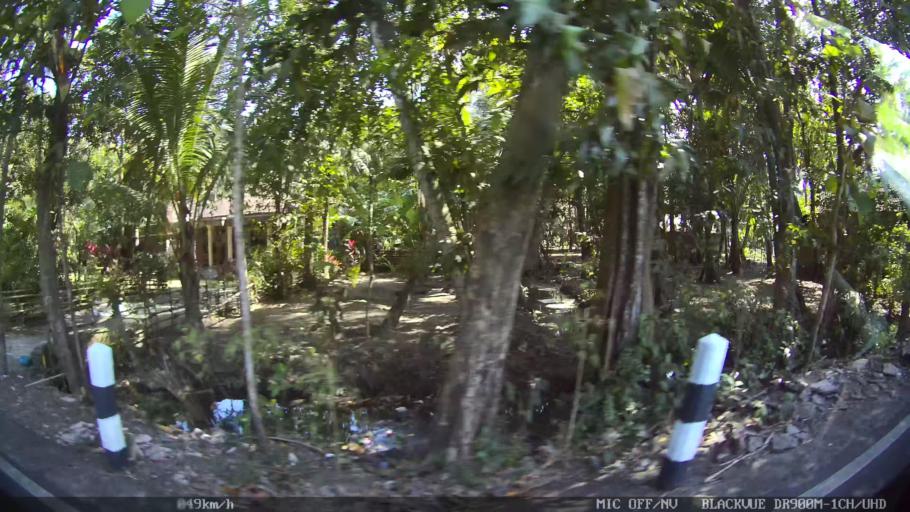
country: ID
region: Daerah Istimewa Yogyakarta
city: Srandakan
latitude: -7.9303
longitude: 110.1931
